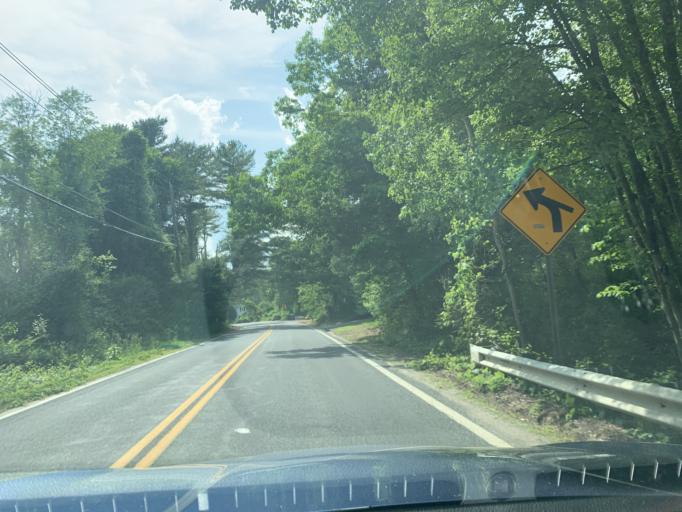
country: US
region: Rhode Island
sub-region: Kent County
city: Coventry
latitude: 41.6933
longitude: -71.7407
